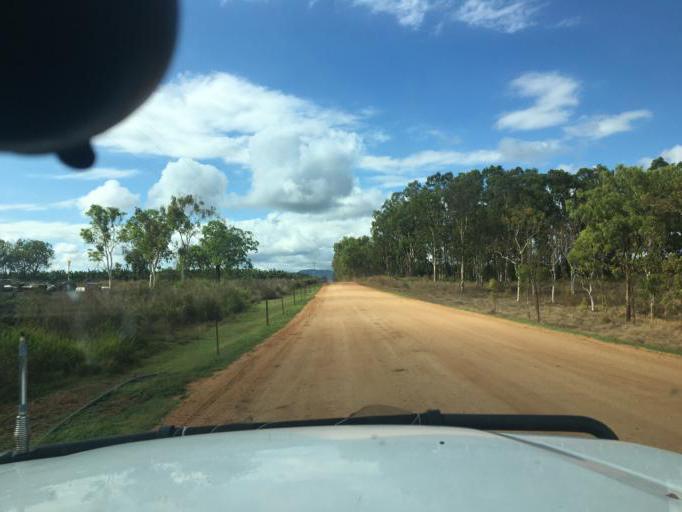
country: AU
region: Queensland
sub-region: Tablelands
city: Mareeba
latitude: -17.0930
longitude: 145.4124
